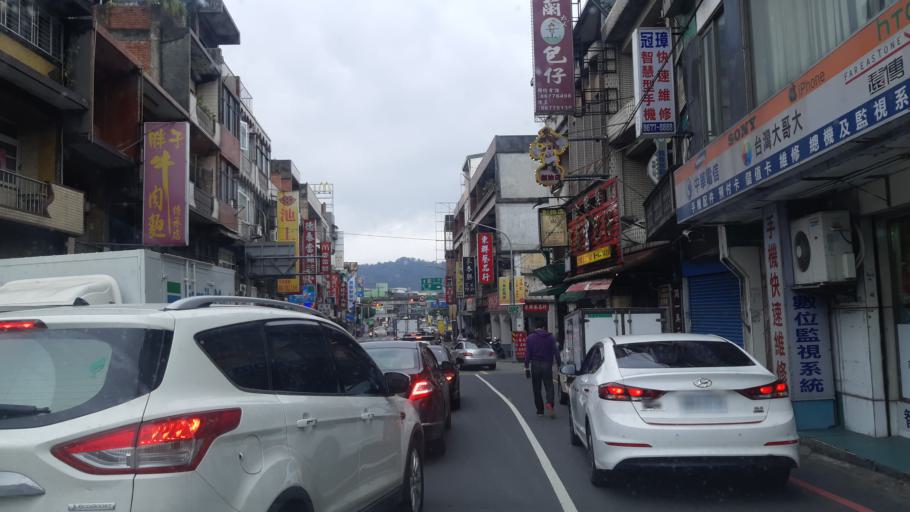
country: TW
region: Taiwan
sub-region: Taoyuan
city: Taoyuan
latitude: 24.9516
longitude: 121.3519
